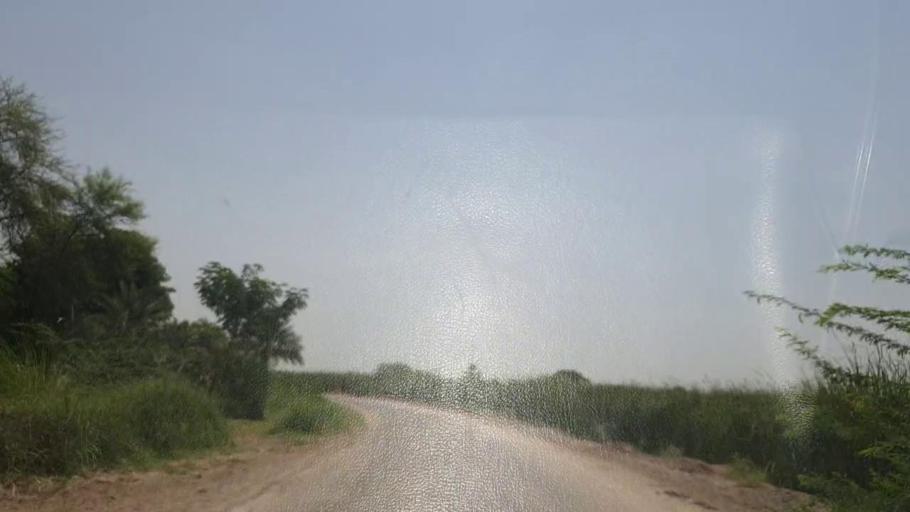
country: PK
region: Sindh
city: Bozdar
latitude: 27.2484
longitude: 68.6618
